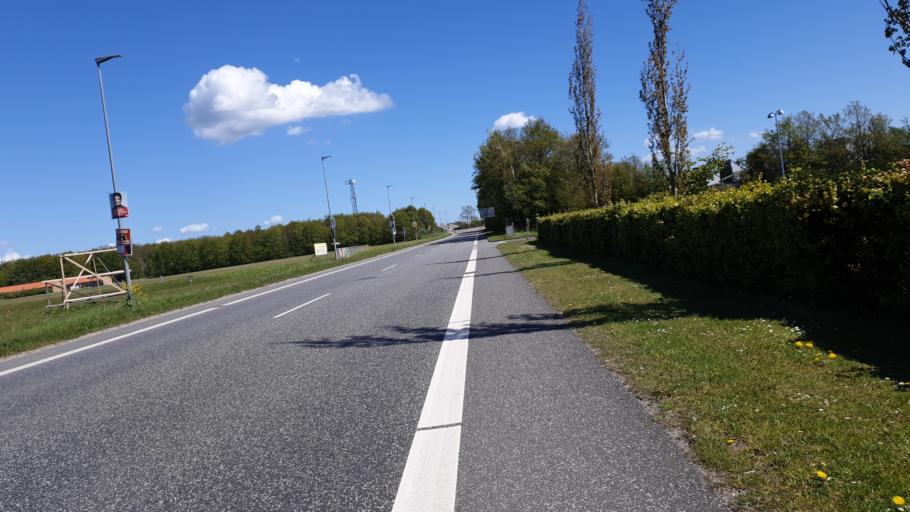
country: DK
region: Central Jutland
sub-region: Hedensted Kommune
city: Hedensted
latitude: 55.7815
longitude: 9.6917
